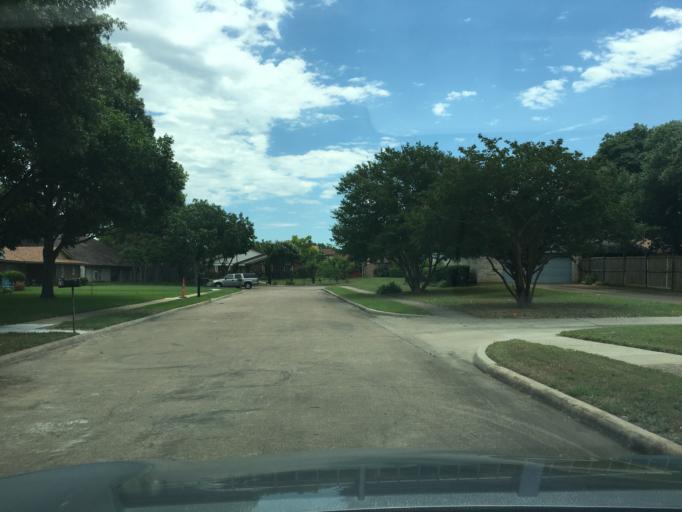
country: US
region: Texas
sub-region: Dallas County
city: Richardson
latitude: 32.9375
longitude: -96.6878
